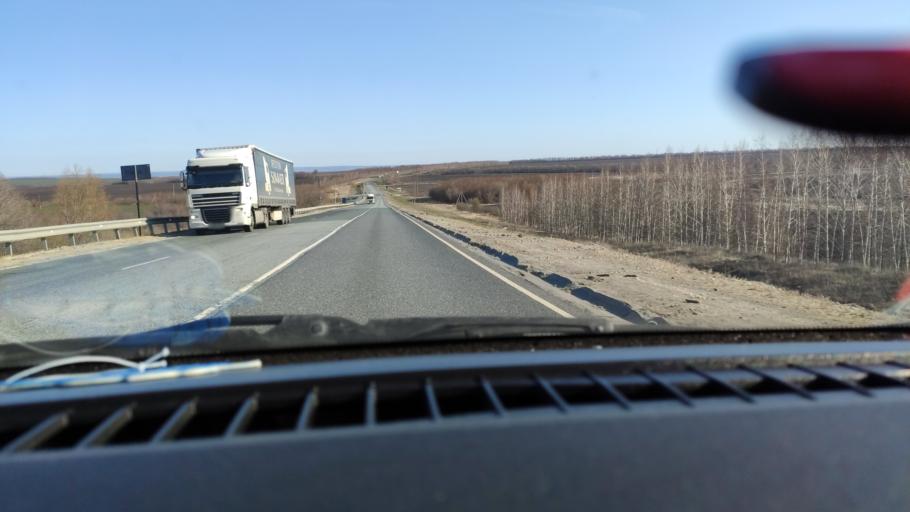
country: RU
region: Samara
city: Syzran'
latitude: 52.9659
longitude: 48.3076
